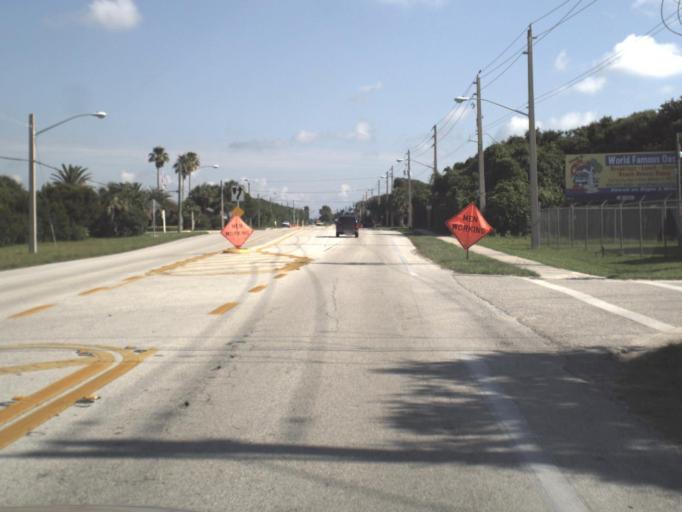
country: US
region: Florida
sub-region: Saint Johns County
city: Butler Beach
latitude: 29.8027
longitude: -81.2650
